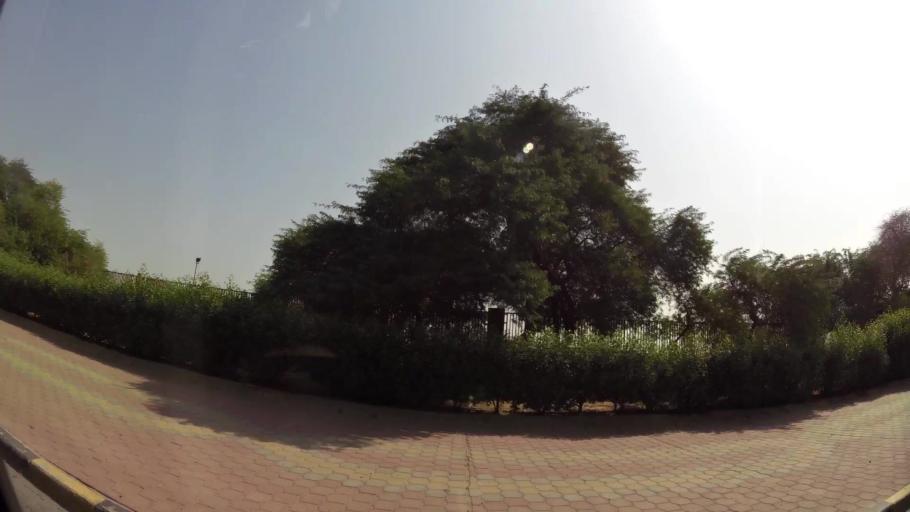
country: KW
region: Al Asimah
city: Ad Dasmah
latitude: 29.3580
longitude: 48.0047
